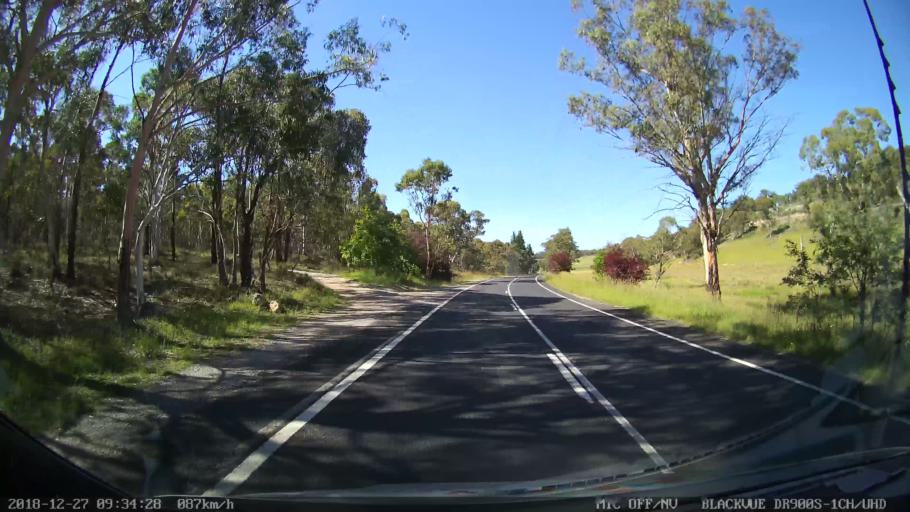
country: AU
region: New South Wales
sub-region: Lithgow
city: Portland
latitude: -33.2266
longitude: 150.0277
